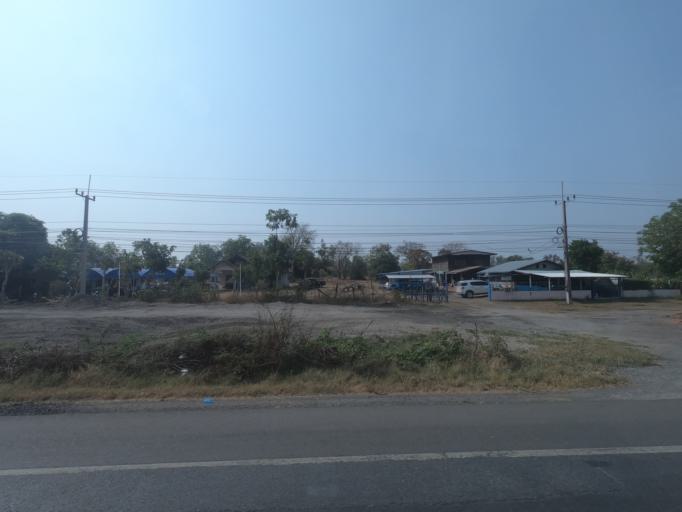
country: TH
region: Nakhon Ratchasima
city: Sida
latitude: 15.5844
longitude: 102.5569
